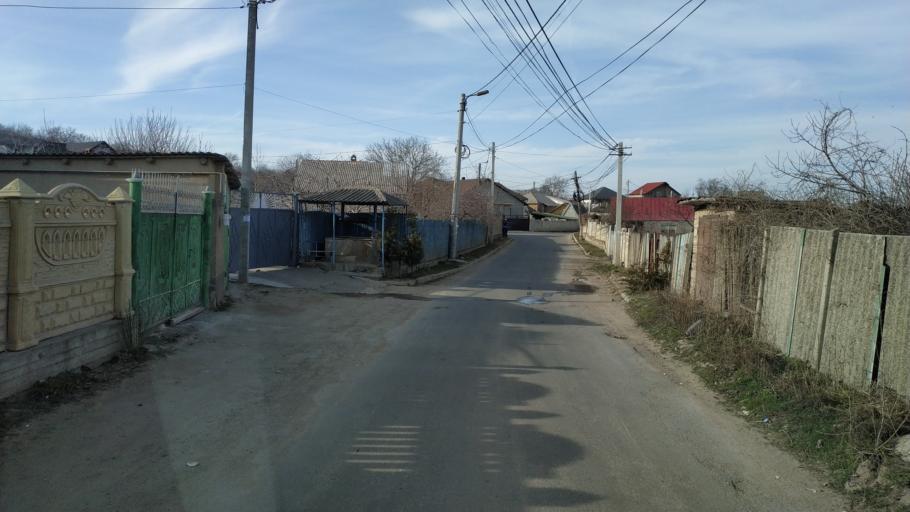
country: MD
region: Chisinau
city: Vatra
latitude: 47.0720
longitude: 28.6725
